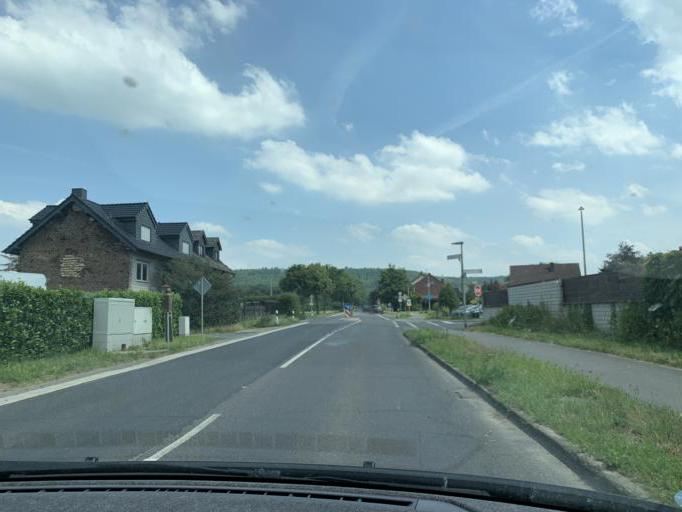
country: DE
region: North Rhine-Westphalia
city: Julich
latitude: 50.9259
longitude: 6.4044
